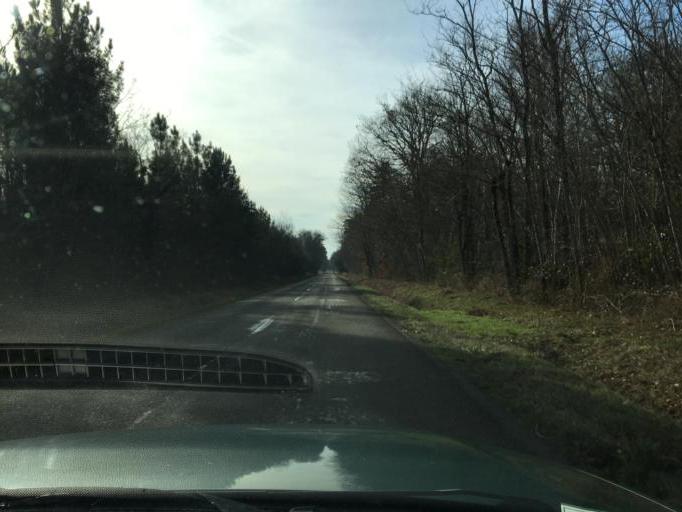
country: FR
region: Centre
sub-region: Departement du Loiret
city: Jouy-le-Potier
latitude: 47.7089
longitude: 1.8566
